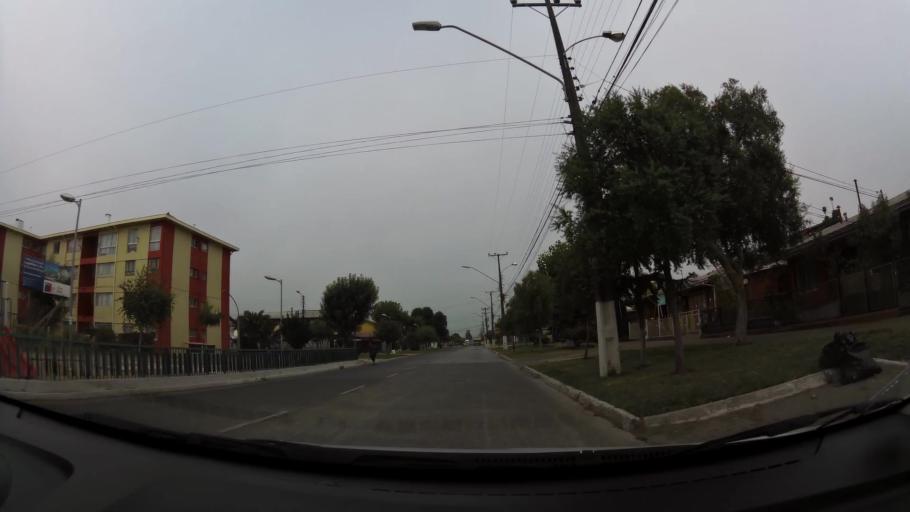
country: CL
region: Biobio
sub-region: Provincia de Concepcion
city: Concepcion
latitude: -36.7947
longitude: -73.0888
